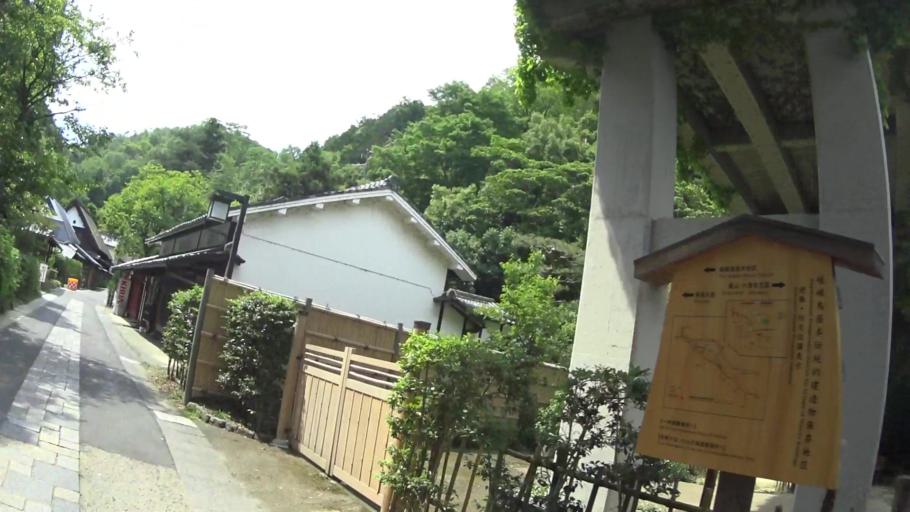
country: JP
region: Kyoto
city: Muko
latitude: 35.0278
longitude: 135.6638
